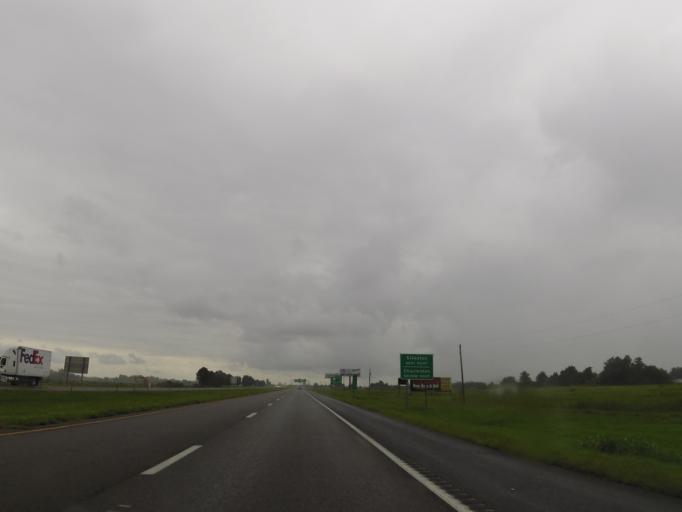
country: US
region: Missouri
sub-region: Scott County
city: Sikeston
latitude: 36.8841
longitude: -89.5335
